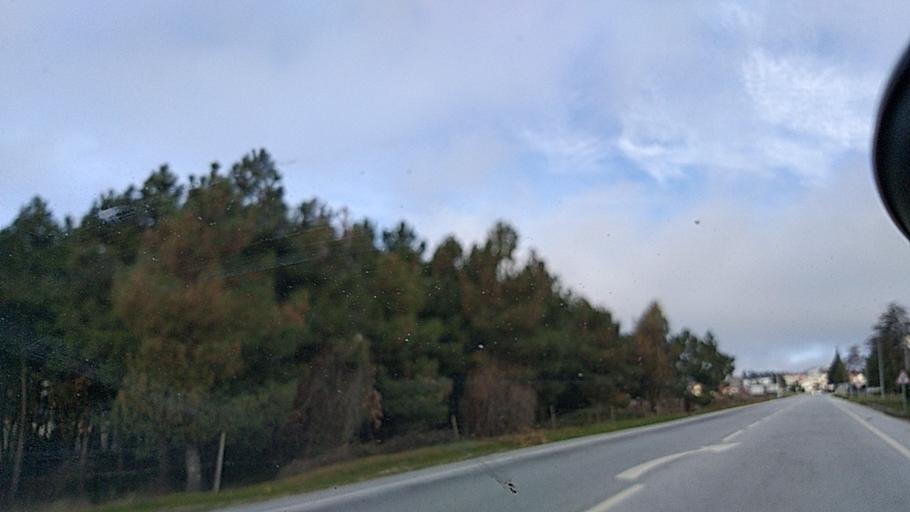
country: PT
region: Guarda
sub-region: Aguiar da Beira
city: Aguiar da Beira
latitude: 40.8153
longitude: -7.5346
